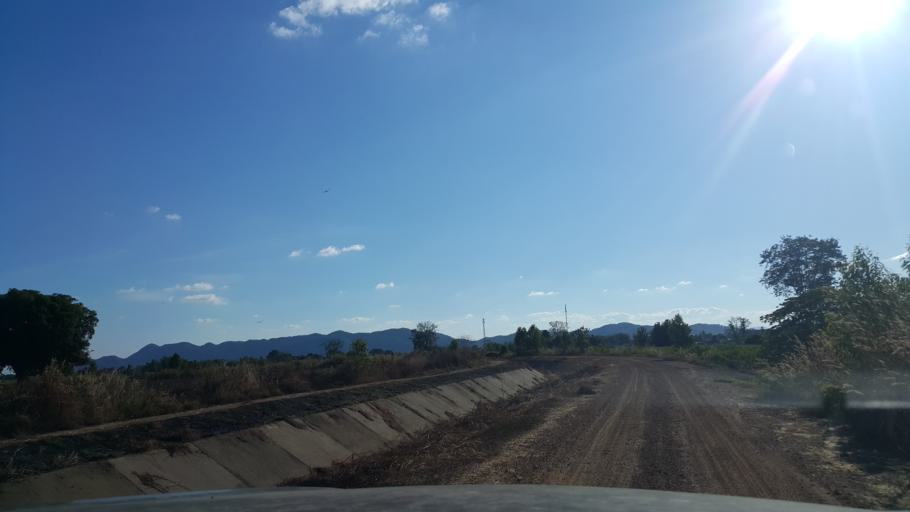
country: TH
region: Sukhothai
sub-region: Amphoe Si Satchanalai
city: Si Satchanalai
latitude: 17.4757
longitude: 99.6569
